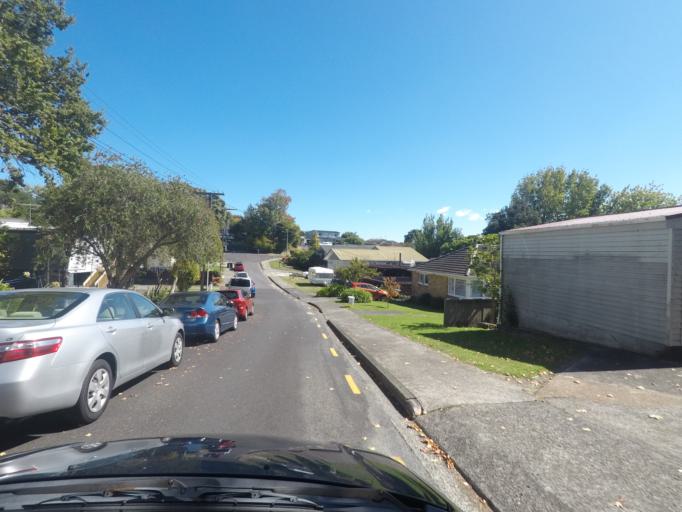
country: NZ
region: Auckland
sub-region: Auckland
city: Rosebank
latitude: -36.8970
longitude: 174.7055
